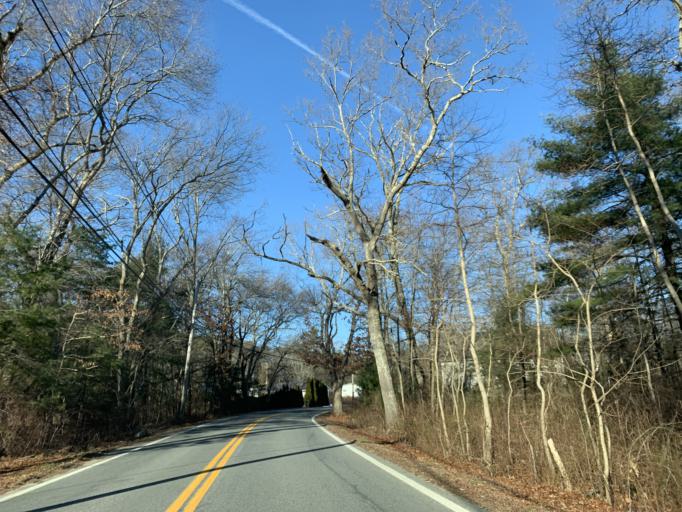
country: US
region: Rhode Island
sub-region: Washington County
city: Exeter
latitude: 41.5678
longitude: -71.5368
